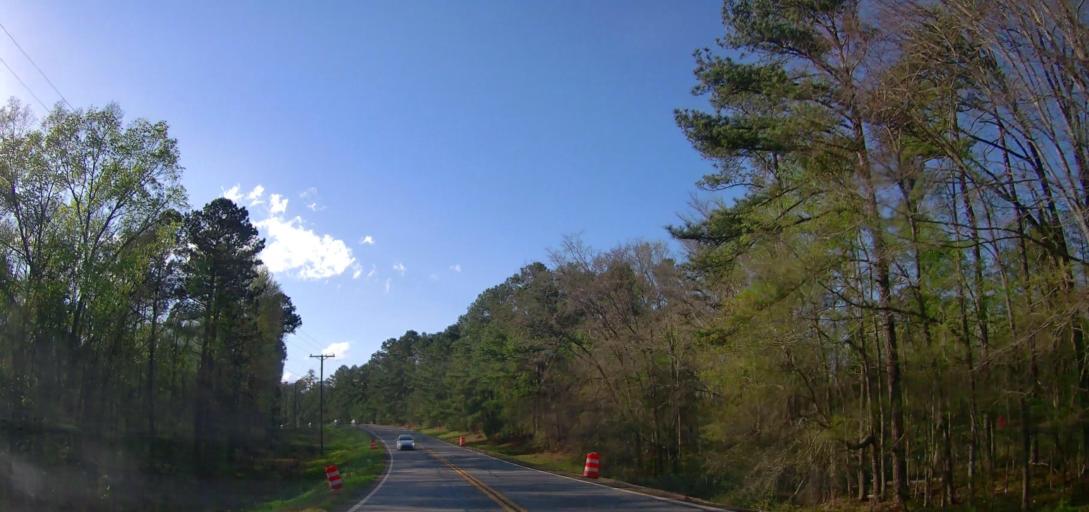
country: US
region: Georgia
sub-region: Baldwin County
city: Milledgeville
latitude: 33.1261
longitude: -83.2982
